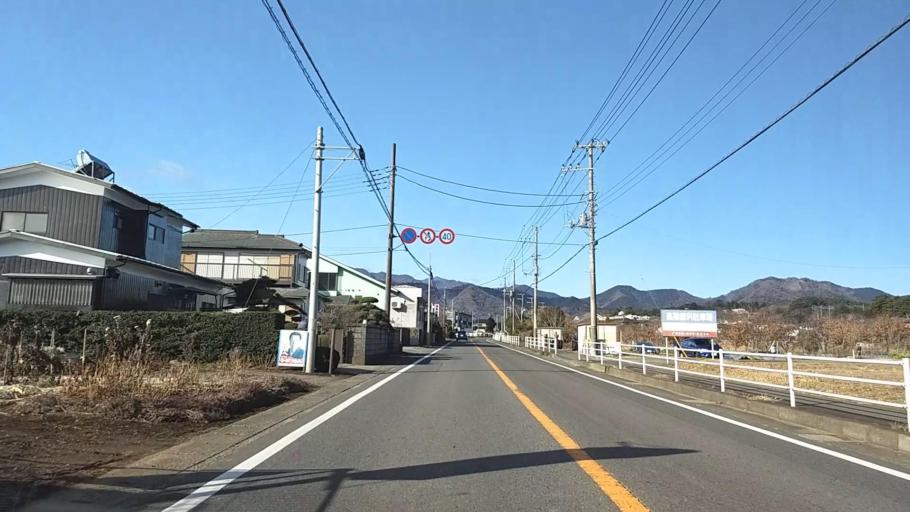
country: JP
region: Kanagawa
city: Atsugi
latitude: 35.4686
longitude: 139.3300
